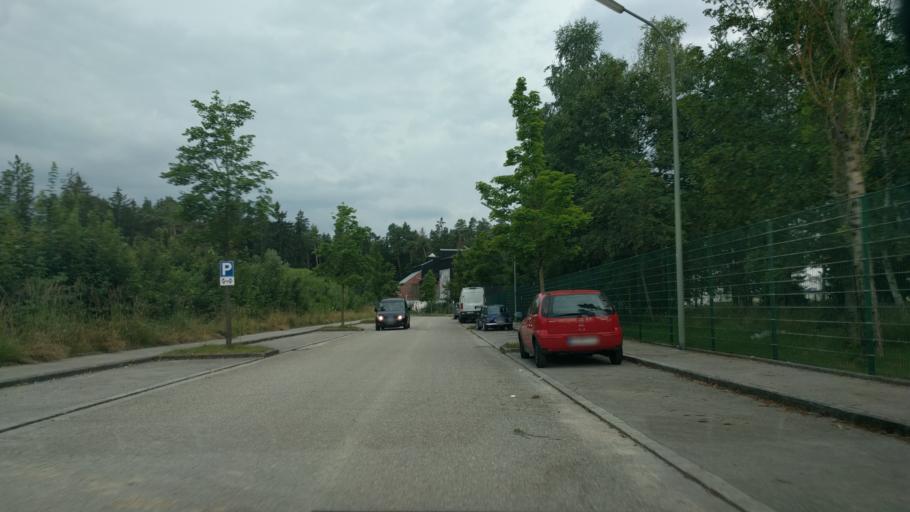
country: DE
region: Bavaria
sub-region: Upper Bavaria
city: Pullach im Isartal
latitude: 48.0640
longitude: 11.5556
